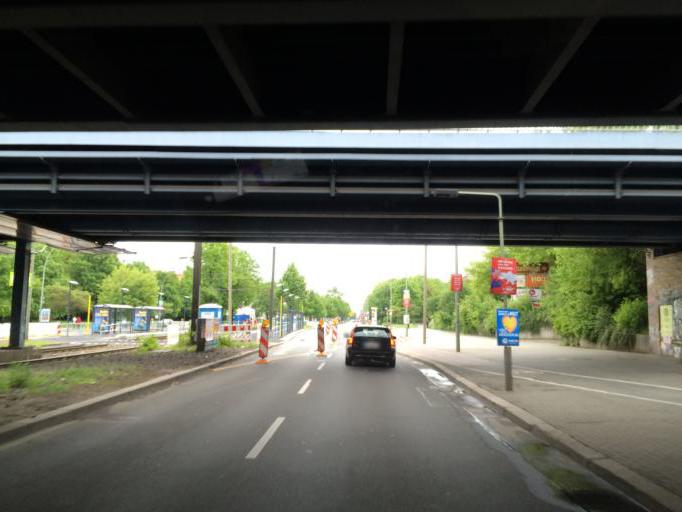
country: DE
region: Berlin
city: Prenzlauer Berg Bezirk
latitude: 52.5406
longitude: 13.4379
